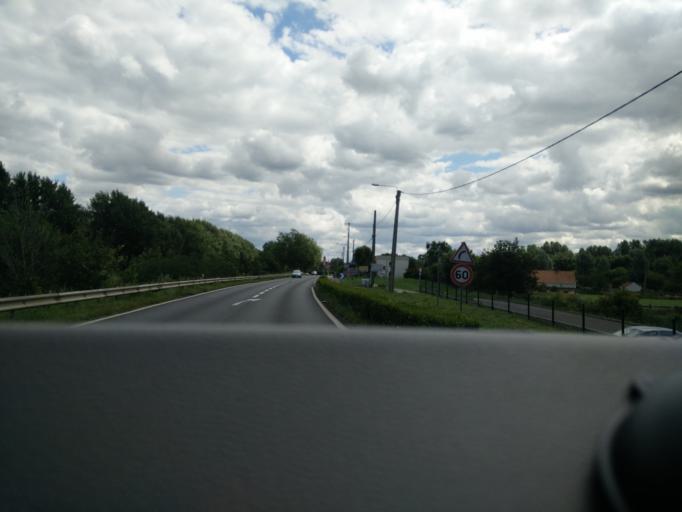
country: FR
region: Nord-Pas-de-Calais
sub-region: Departement du Nord
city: Bergues
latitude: 50.9754
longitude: 2.4214
